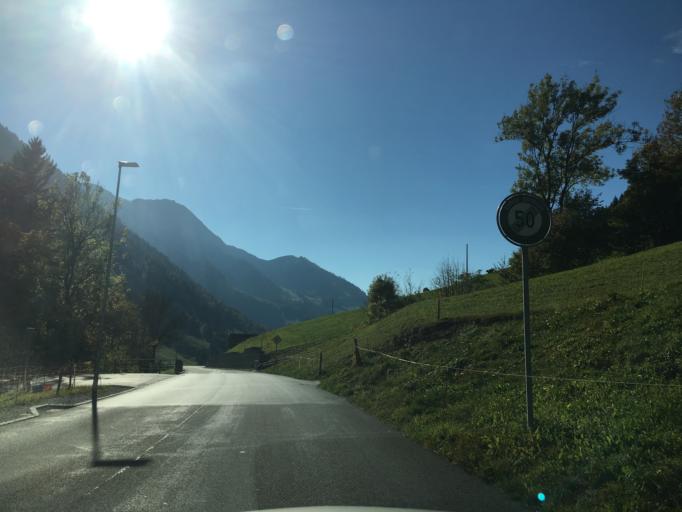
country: CH
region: Fribourg
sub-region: Gruyere District
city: Charmey
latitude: 46.6095
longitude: 7.2680
